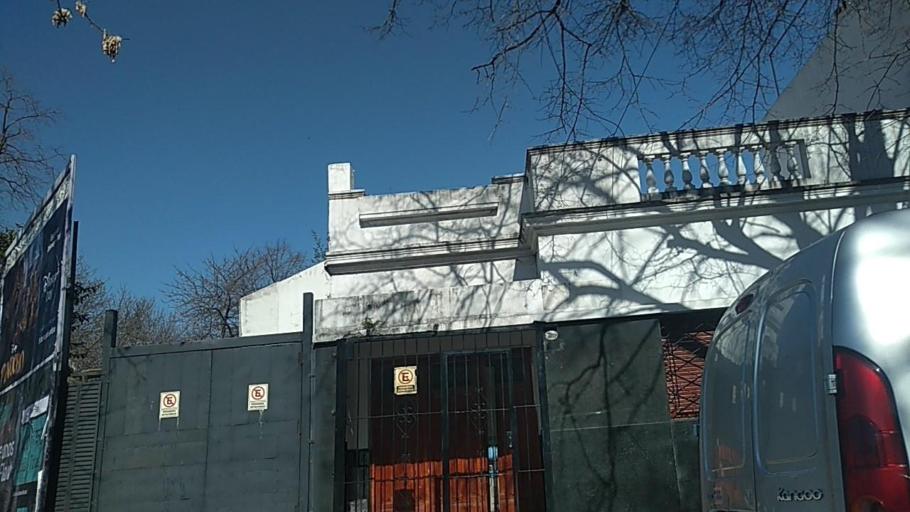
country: AR
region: Buenos Aires F.D.
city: Villa Santa Rita
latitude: -34.6050
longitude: -58.5060
